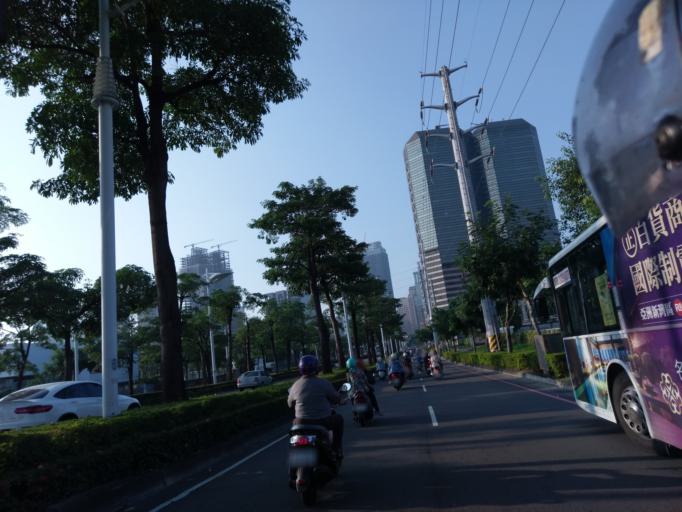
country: TW
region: Kaohsiung
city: Kaohsiung
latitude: 22.6025
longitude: 120.3111
